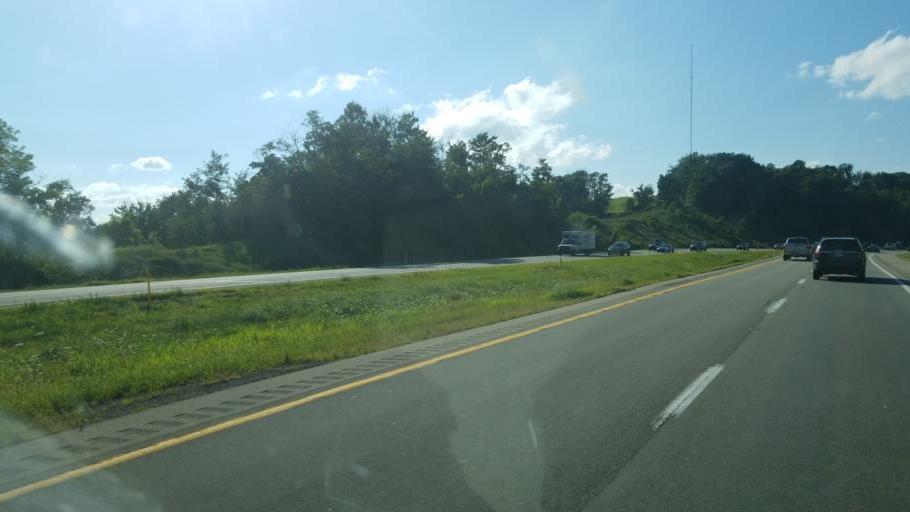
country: US
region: Pennsylvania
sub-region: Greene County
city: Morrisville
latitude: 39.8680
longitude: -80.1285
